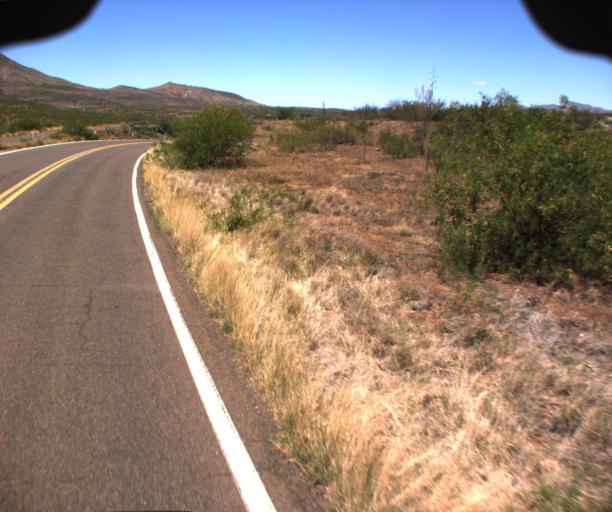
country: US
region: Arizona
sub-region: Cochise County
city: Douglas
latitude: 31.4593
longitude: -109.3775
